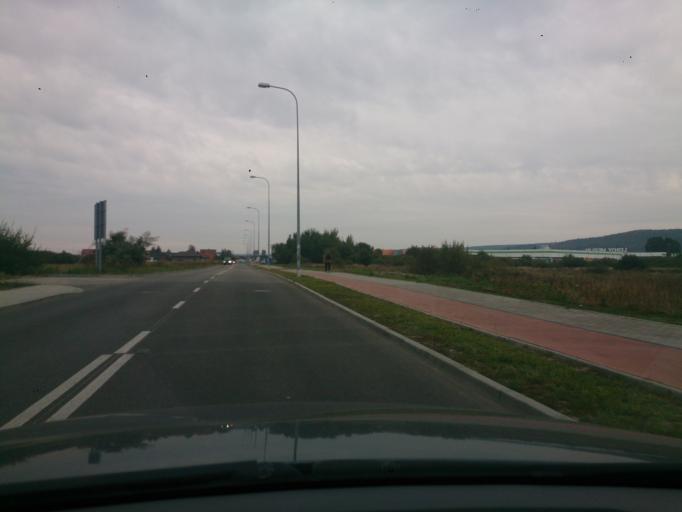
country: PL
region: Pomeranian Voivodeship
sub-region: Powiat wejherowski
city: Reda
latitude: 54.5907
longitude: 18.3684
